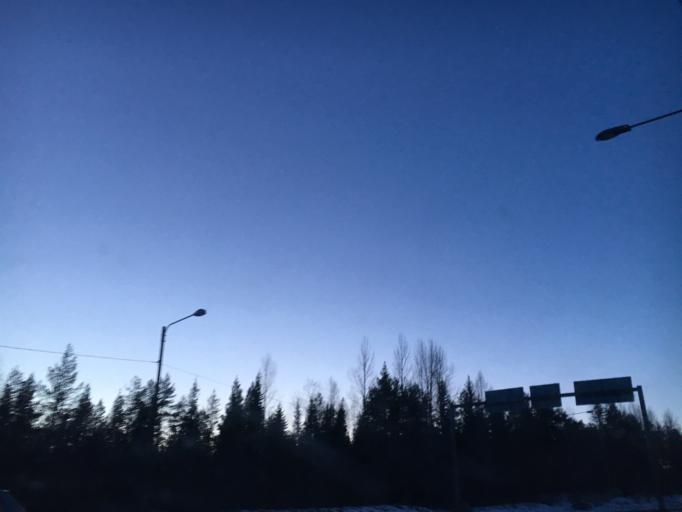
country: FI
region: Kainuu
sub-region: Kajaani
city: Kajaani
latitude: 64.1958
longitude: 27.7513
